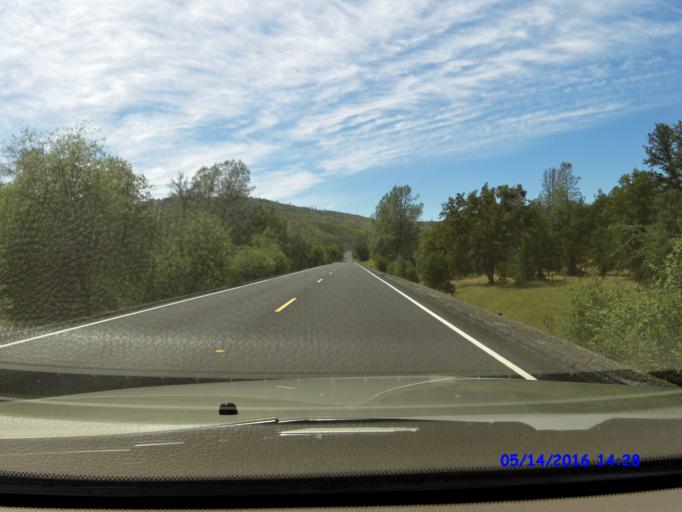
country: US
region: California
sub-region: Tuolumne County
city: Tuolumne City
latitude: 37.7338
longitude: -120.2194
